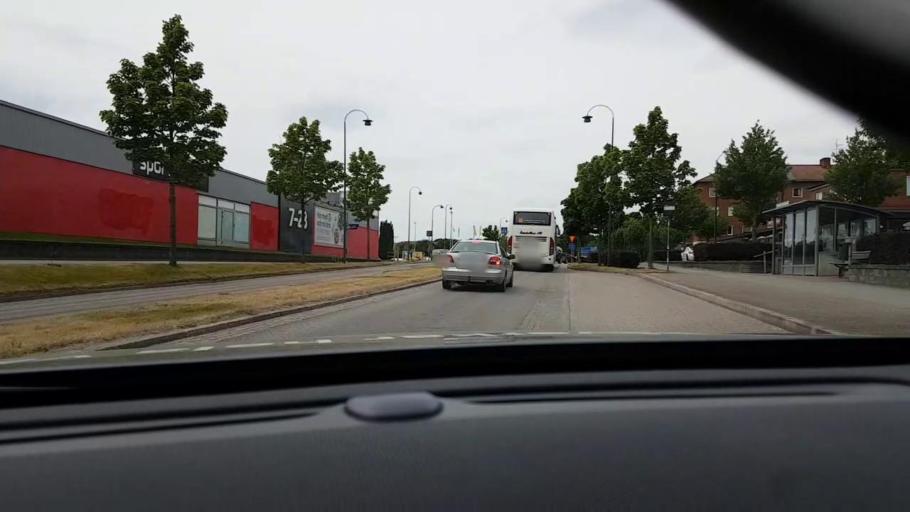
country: SE
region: Skane
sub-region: Hassleholms Kommun
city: Hassleholm
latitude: 56.1550
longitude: 13.7606
